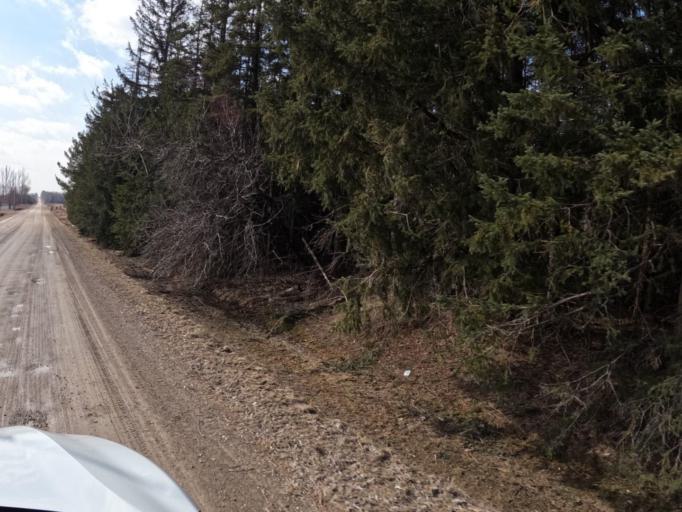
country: CA
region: Ontario
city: Orangeville
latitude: 43.9097
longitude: -80.2530
